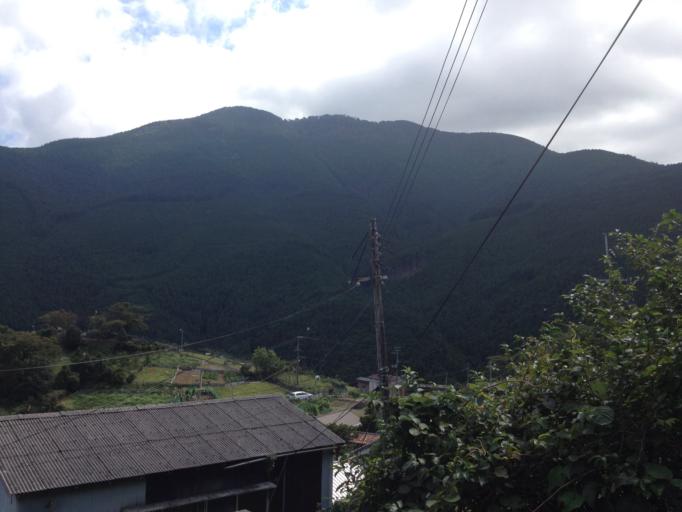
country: JP
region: Nara
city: Yoshino-cho
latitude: 34.3239
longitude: 135.9483
